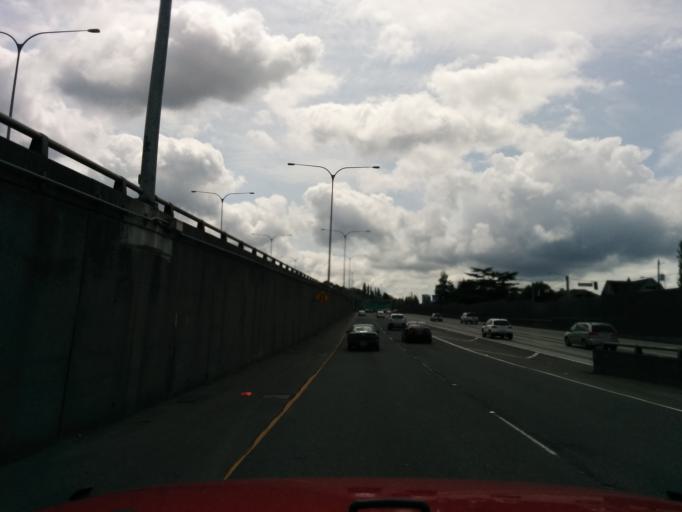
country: US
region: Washington
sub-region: King County
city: Seattle
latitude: 47.6406
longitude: -122.3231
